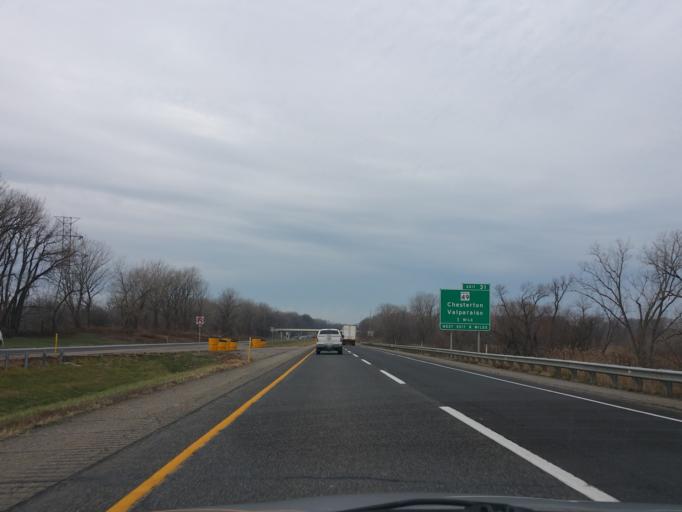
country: US
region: Indiana
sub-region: Porter County
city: Chesterton
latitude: 41.5716
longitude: -87.0209
